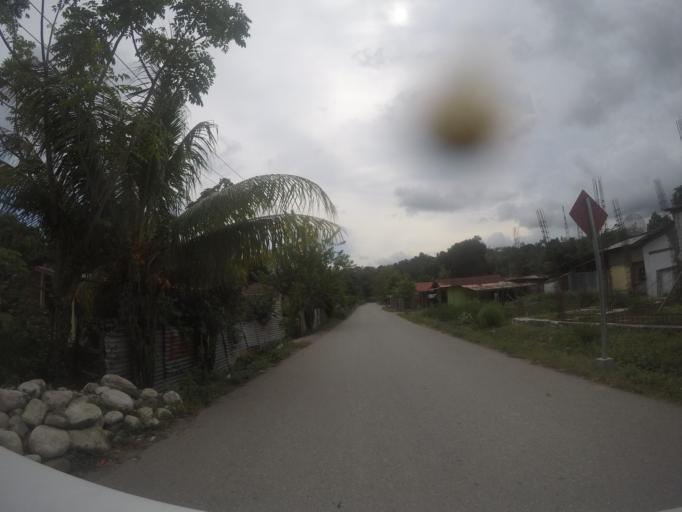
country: TL
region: Viqueque
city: Viqueque
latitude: -8.8711
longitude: 126.3659
